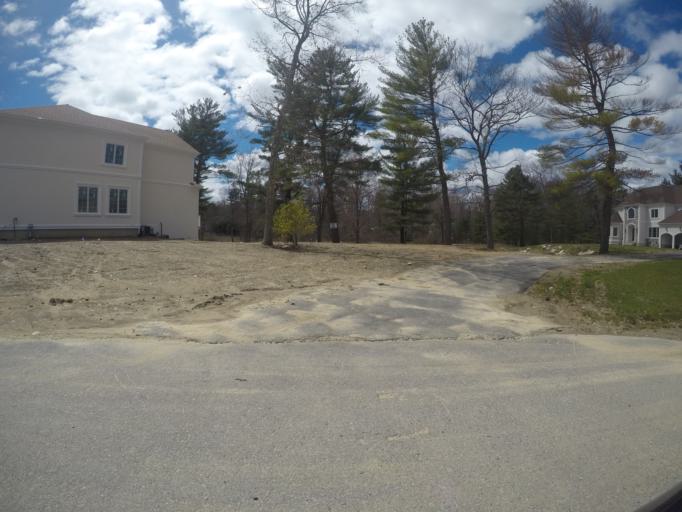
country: US
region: Massachusetts
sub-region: Norfolk County
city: Stoughton
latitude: 42.0774
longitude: -71.0832
